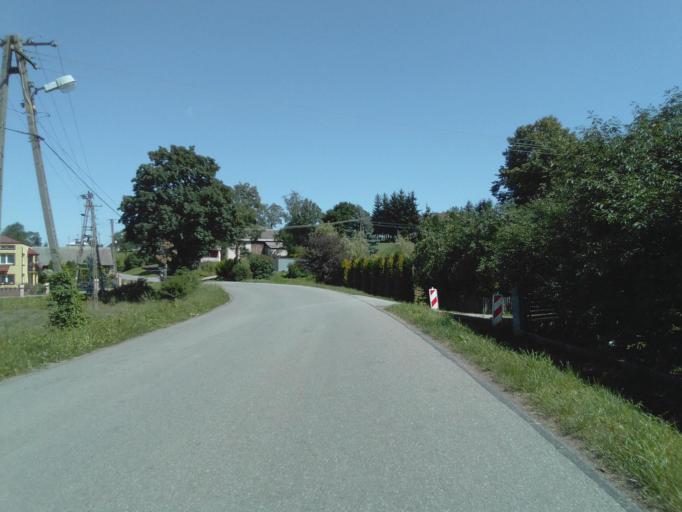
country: PL
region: Subcarpathian Voivodeship
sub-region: Powiat krosnienski
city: Chorkowka
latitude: 49.6664
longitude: 21.6120
